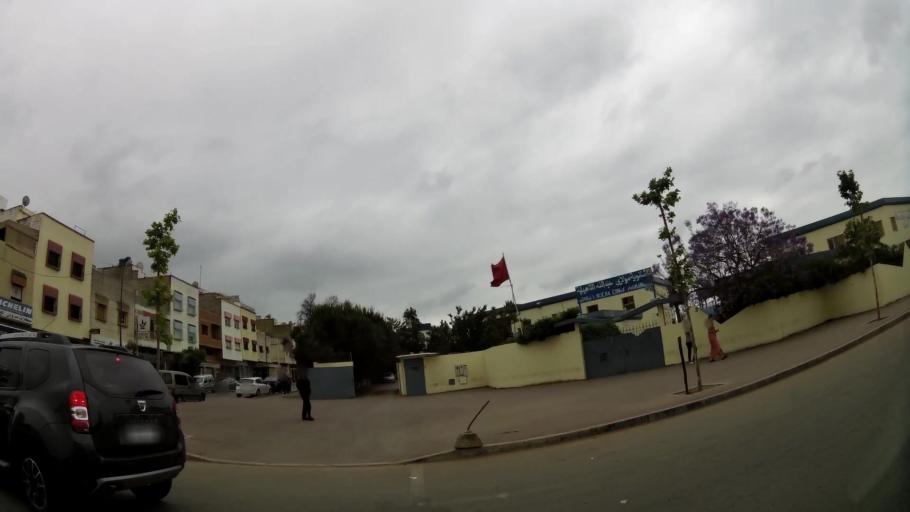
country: MA
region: Rabat-Sale-Zemmour-Zaer
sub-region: Rabat
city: Rabat
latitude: 33.9747
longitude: -6.8177
